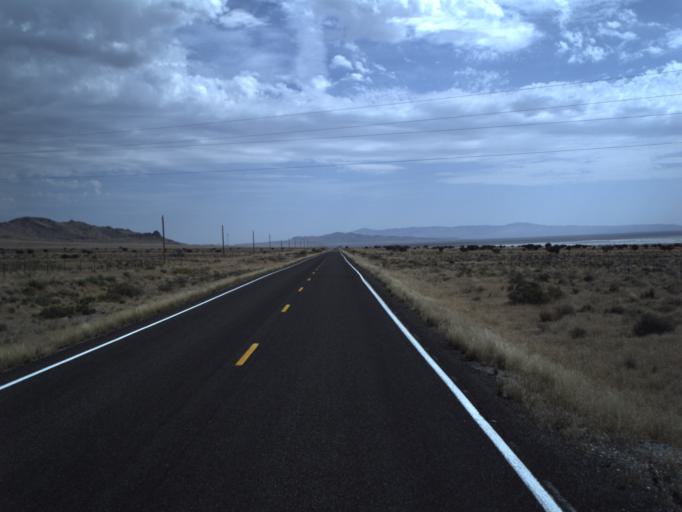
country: US
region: Utah
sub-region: Tooele County
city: Wendover
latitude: 41.4369
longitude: -113.7425
